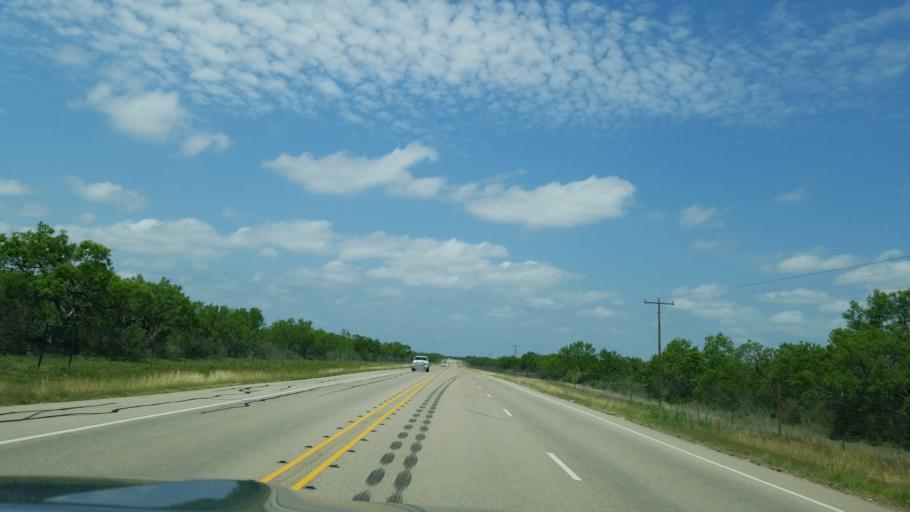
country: US
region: Texas
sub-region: Frio County
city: Pearsall
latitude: 29.0076
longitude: -99.1840
